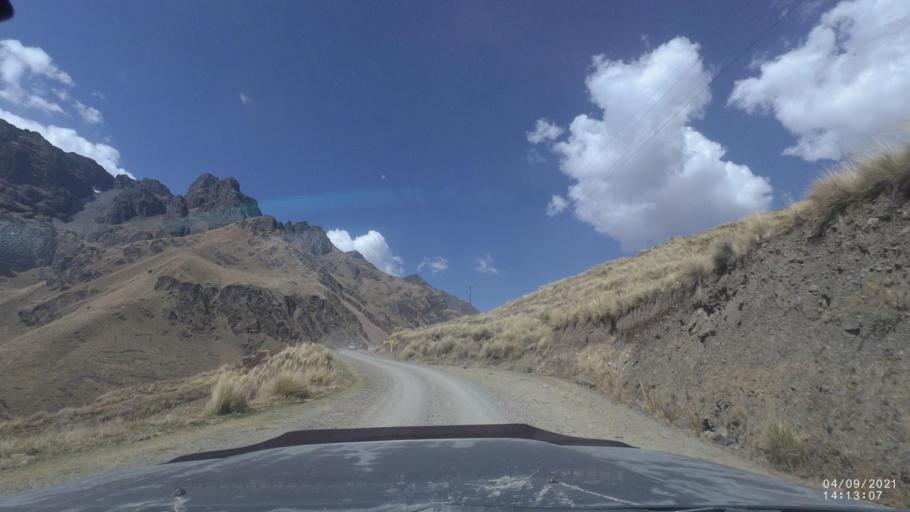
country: BO
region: Cochabamba
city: Sipe Sipe
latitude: -17.2239
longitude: -66.4494
